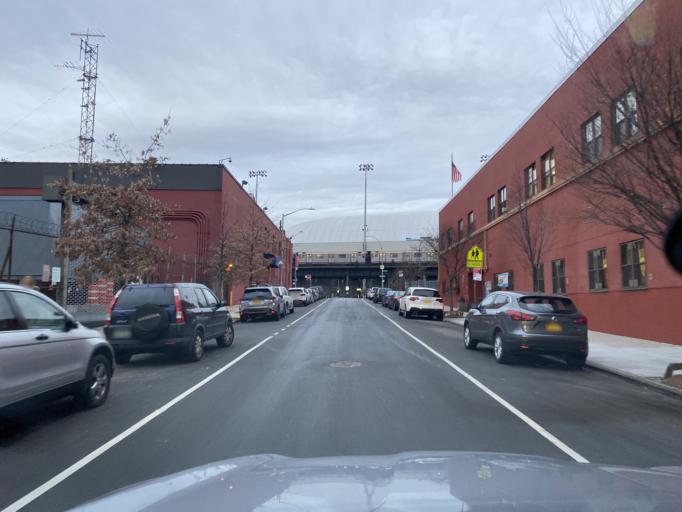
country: US
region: New York
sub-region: New York County
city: Inwood
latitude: 40.8713
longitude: -73.9123
